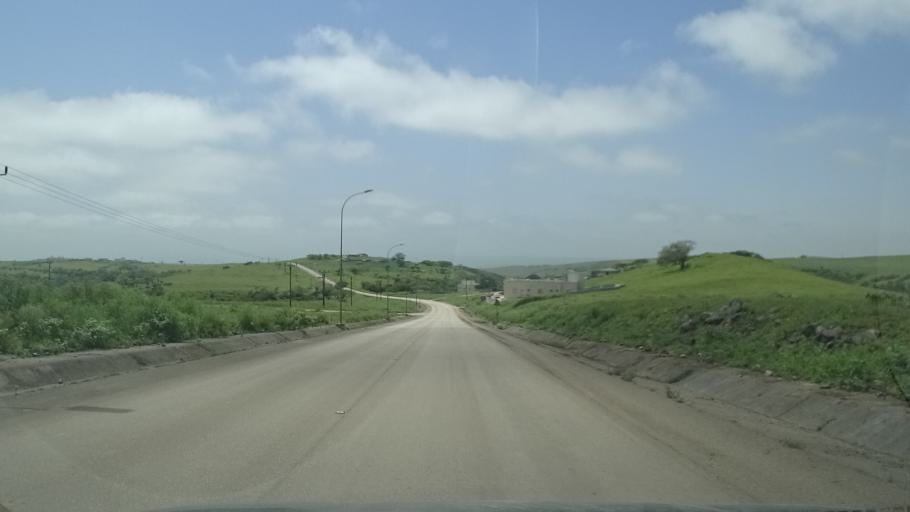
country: OM
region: Zufar
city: Salalah
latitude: 17.2209
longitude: 54.2628
